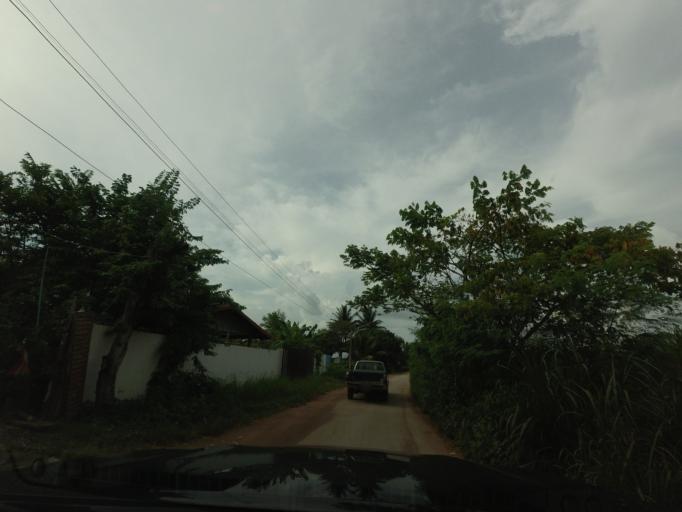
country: TH
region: Changwat Nong Bua Lamphu
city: Suwannakhuha
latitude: 17.4172
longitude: 102.3343
